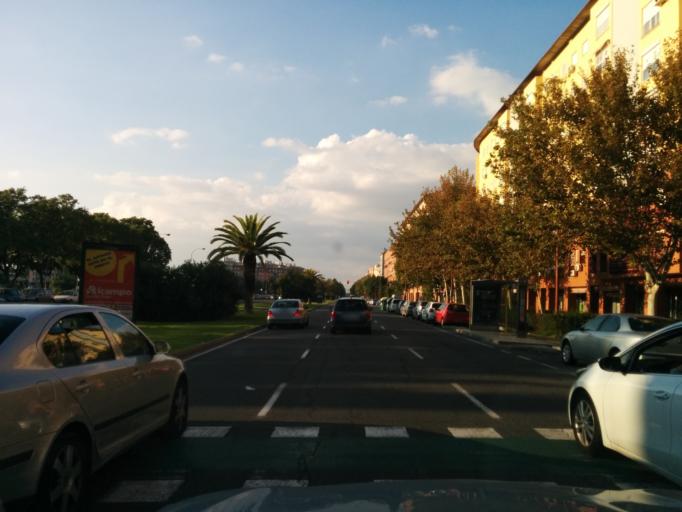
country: ES
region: Andalusia
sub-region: Provincia de Sevilla
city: Sevilla
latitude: 37.3933
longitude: -5.9206
